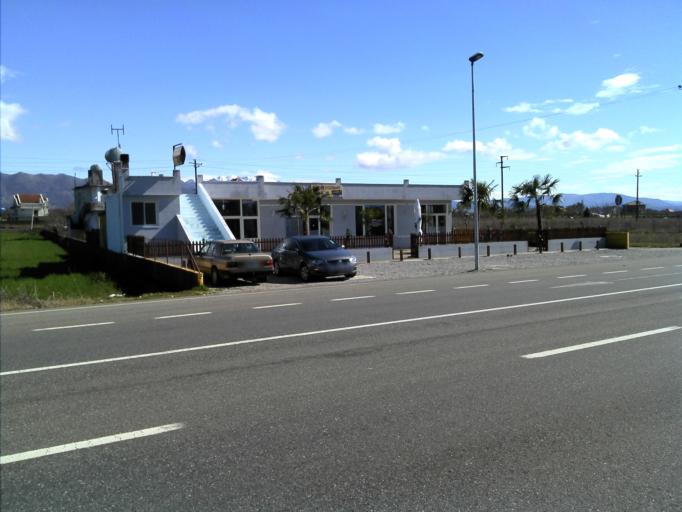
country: AL
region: Shkoder
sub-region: Rrethi i Malesia e Madhe
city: Grude-Fushe
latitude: 42.1440
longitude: 19.4814
